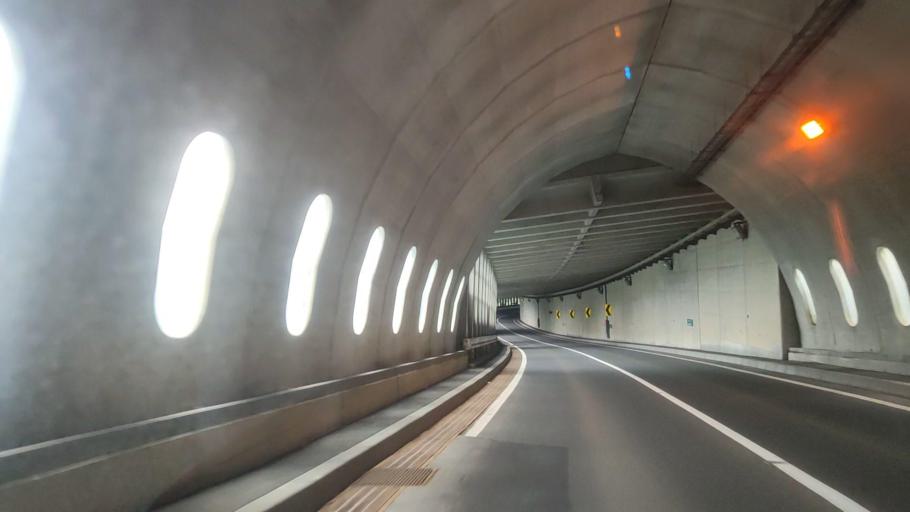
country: JP
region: Hokkaido
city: Otaru
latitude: 43.0785
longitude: 141.0865
